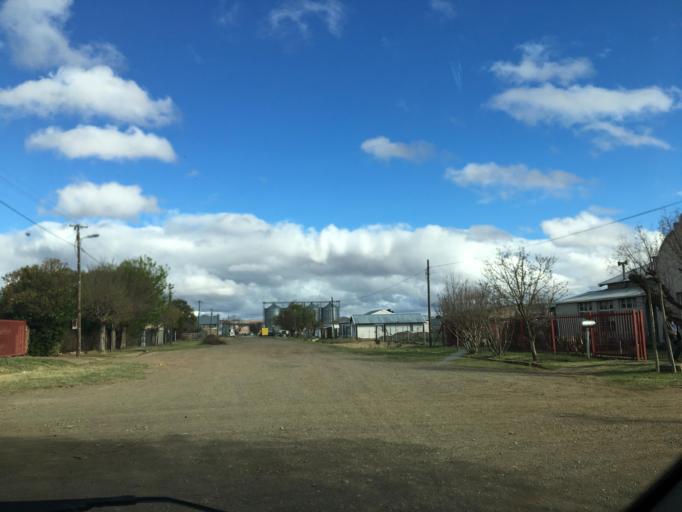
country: ZA
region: Eastern Cape
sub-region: Chris Hani District Municipality
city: Elliot
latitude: -31.3319
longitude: 27.8457
